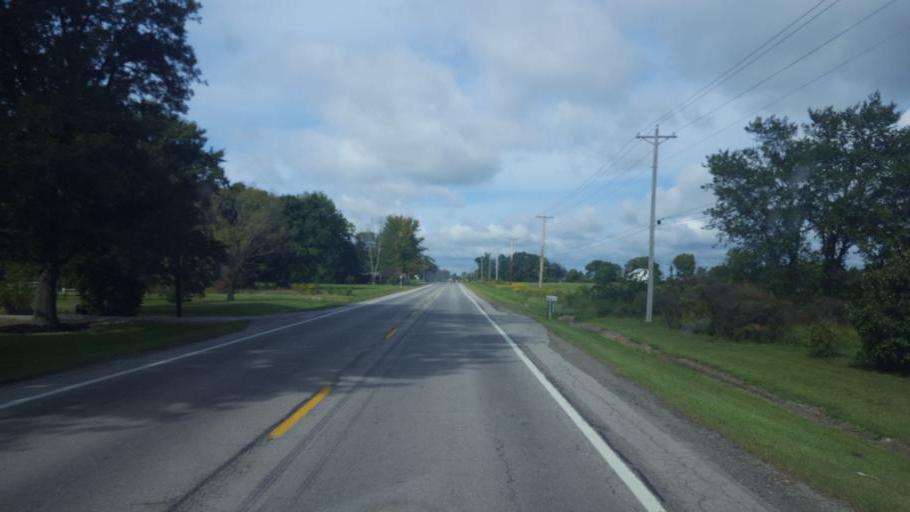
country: US
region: Ohio
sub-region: Lorain County
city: Wellington
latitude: 41.1688
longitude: -82.1473
